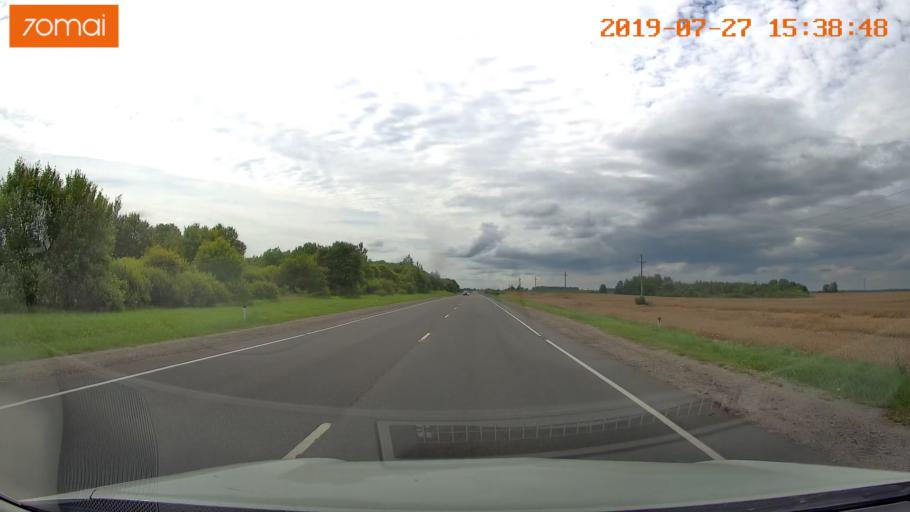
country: RU
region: Kaliningrad
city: Gusev
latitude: 54.6070
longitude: 22.3047
